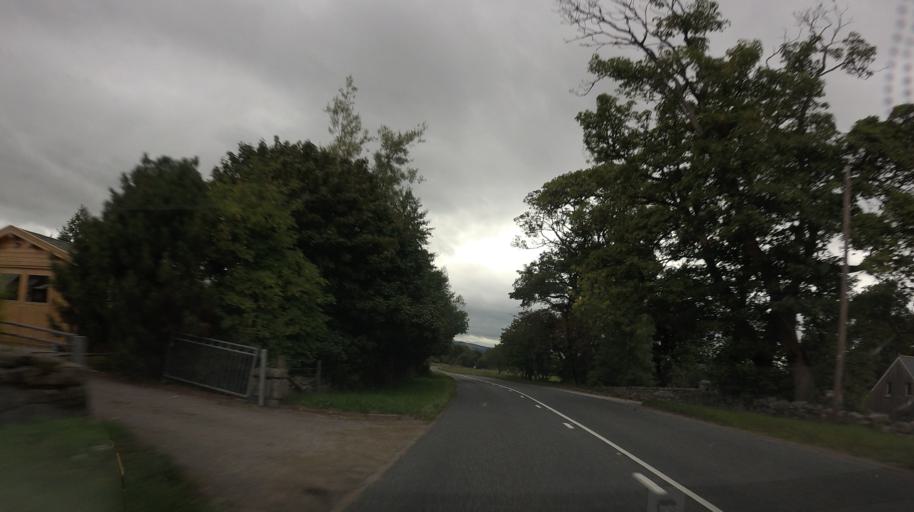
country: GB
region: Scotland
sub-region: Aberdeenshire
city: Kemnay
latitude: 57.1829
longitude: -2.4738
